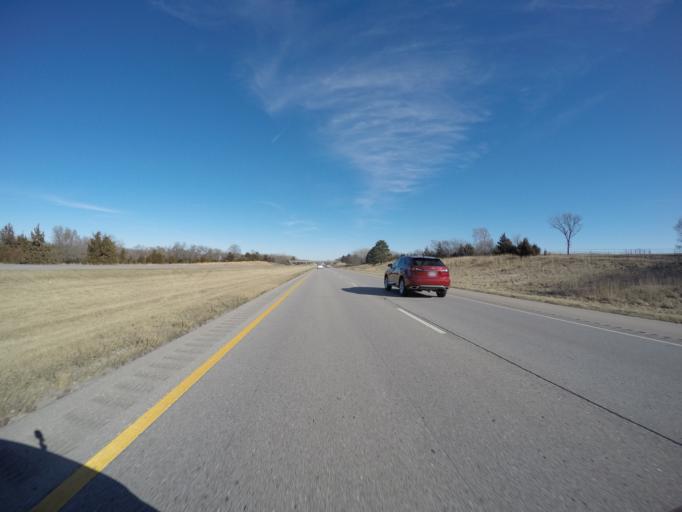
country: US
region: Nebraska
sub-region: Seward County
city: Milford
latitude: 40.8203
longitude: -96.8978
